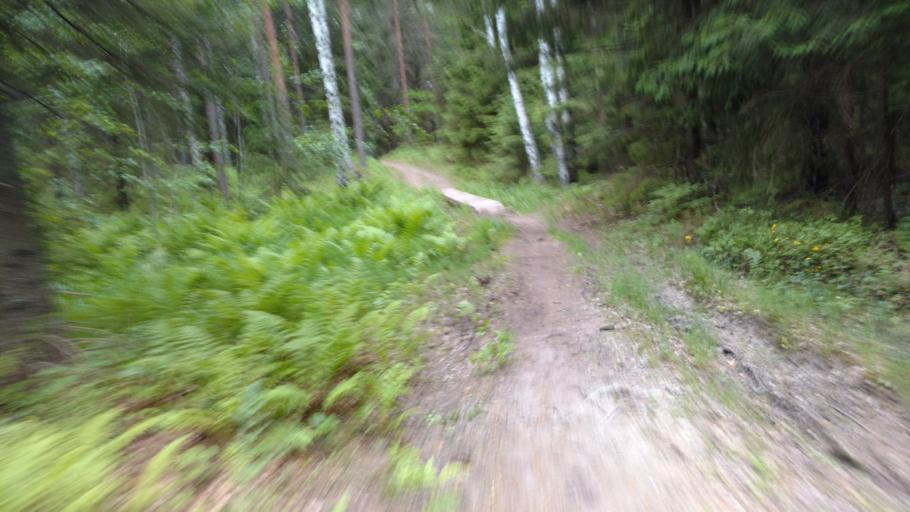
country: FI
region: Uusimaa
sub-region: Raaseporin
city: Pohja
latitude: 60.1184
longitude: 23.5646
